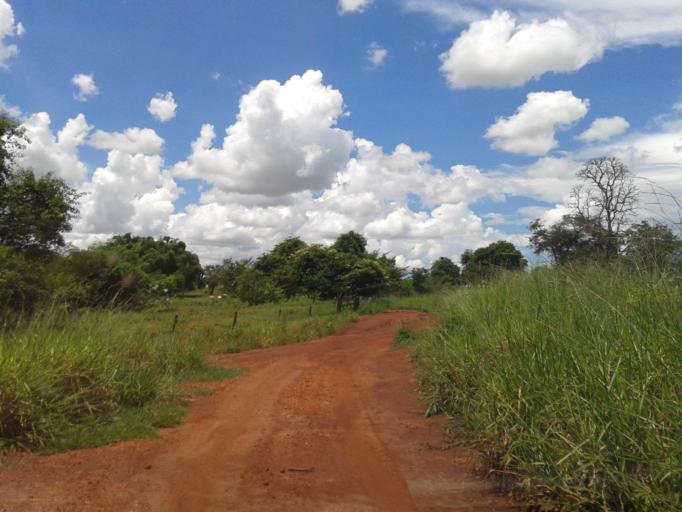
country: BR
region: Minas Gerais
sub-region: Capinopolis
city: Capinopolis
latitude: -18.7938
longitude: -49.8355
